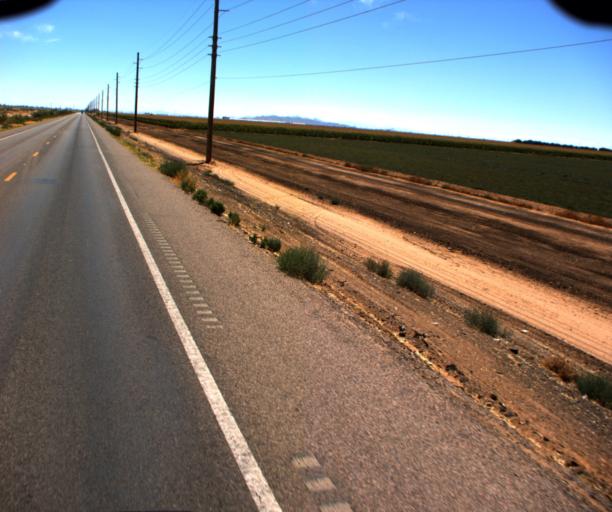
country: US
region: Arizona
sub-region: Pinal County
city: Casa Grande
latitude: 32.8794
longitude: -111.9439
